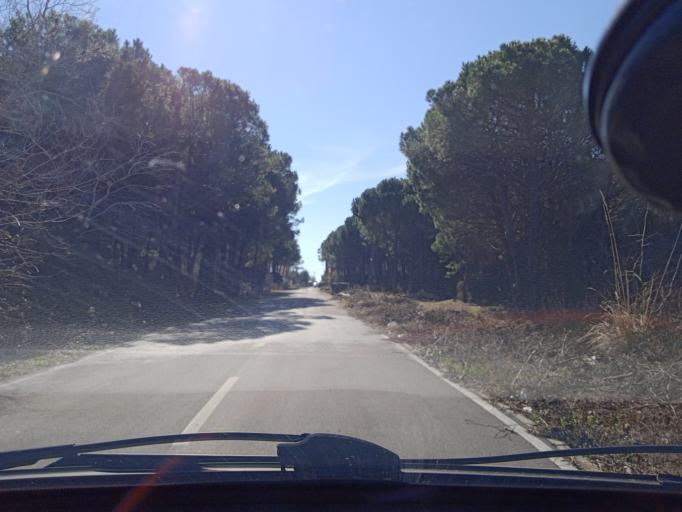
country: AL
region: Shkoder
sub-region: Rrethi i Shkodres
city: Velipoje
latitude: 41.8654
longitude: 19.4156
